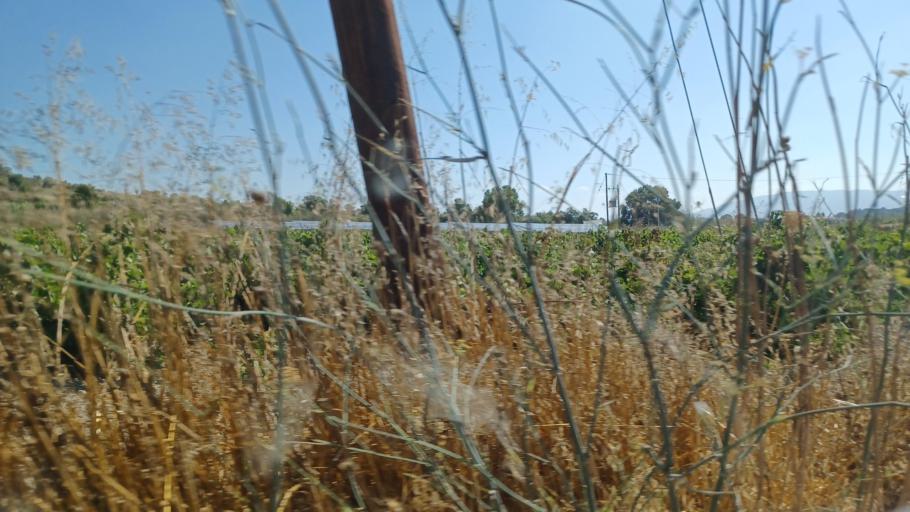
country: CY
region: Pafos
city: Tala
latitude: 34.8906
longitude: 32.4984
